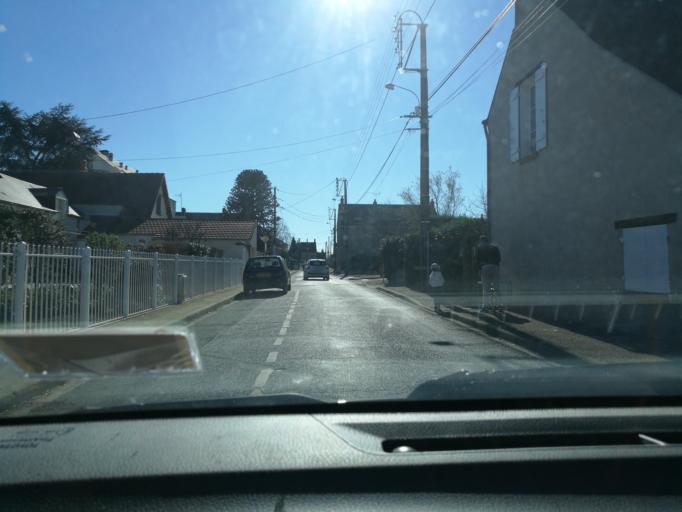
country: FR
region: Centre
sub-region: Departement du Loiret
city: Saint-Pryve-Saint-Mesmin
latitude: 47.8887
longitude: 1.8871
